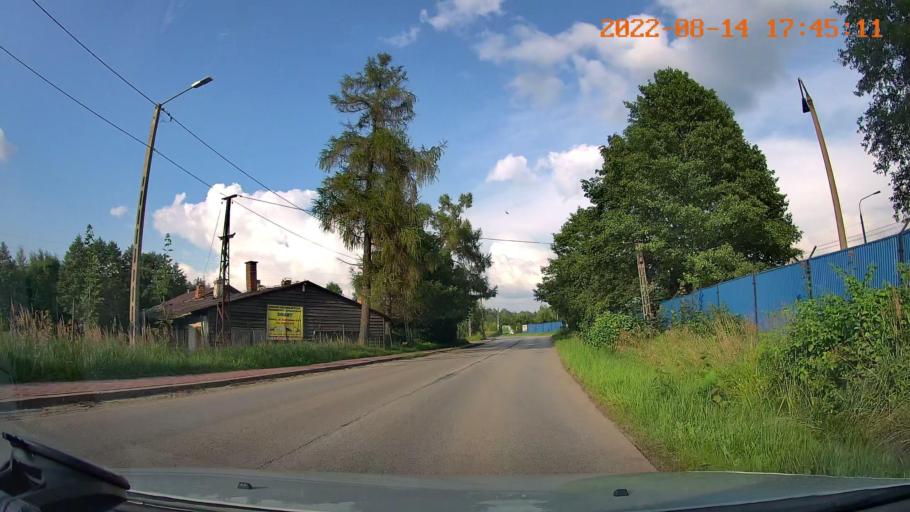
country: PL
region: Swietokrzyskie
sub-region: Powiat kielecki
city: Zagnansk
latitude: 50.9746
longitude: 20.6554
